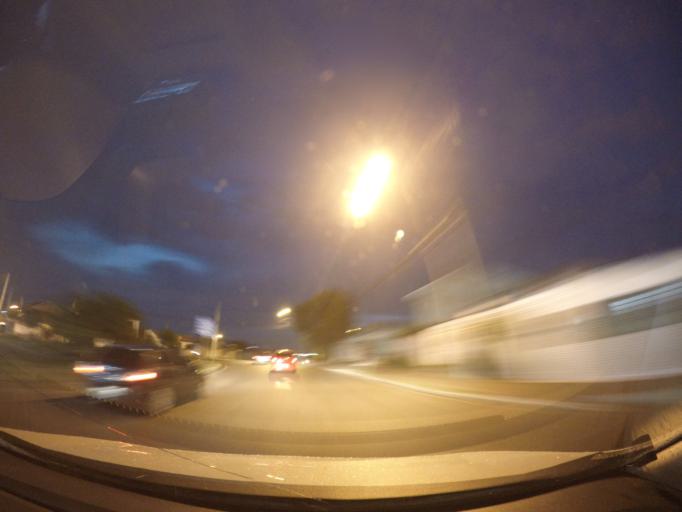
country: BR
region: Parana
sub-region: Curitiba
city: Curitiba
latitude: -25.4702
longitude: -49.2626
